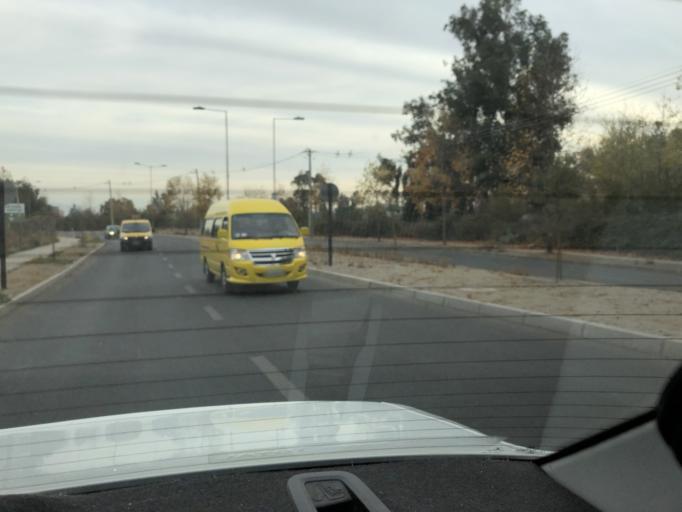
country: CL
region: Santiago Metropolitan
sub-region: Provincia de Cordillera
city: Puente Alto
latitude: -33.5942
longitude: -70.5100
